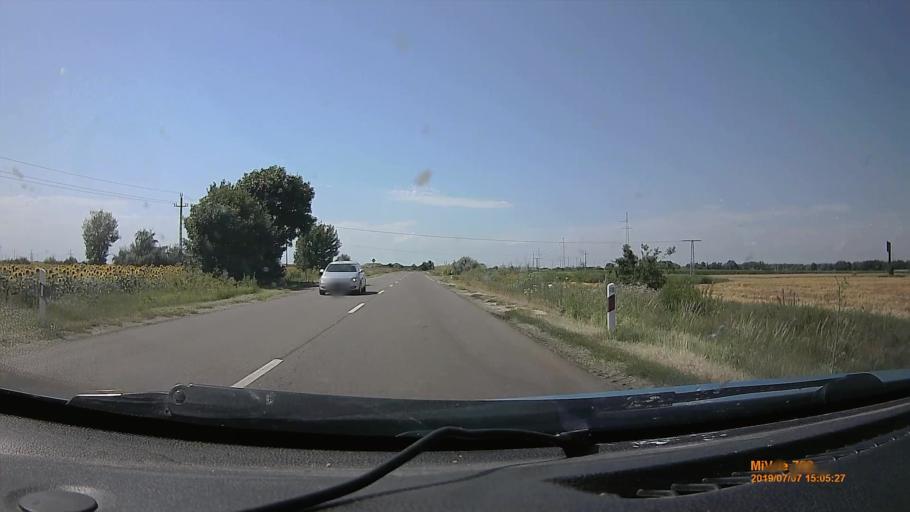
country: HU
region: Jasz-Nagykun-Szolnok
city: Zagyvarekas
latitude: 47.2090
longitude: 20.1455
